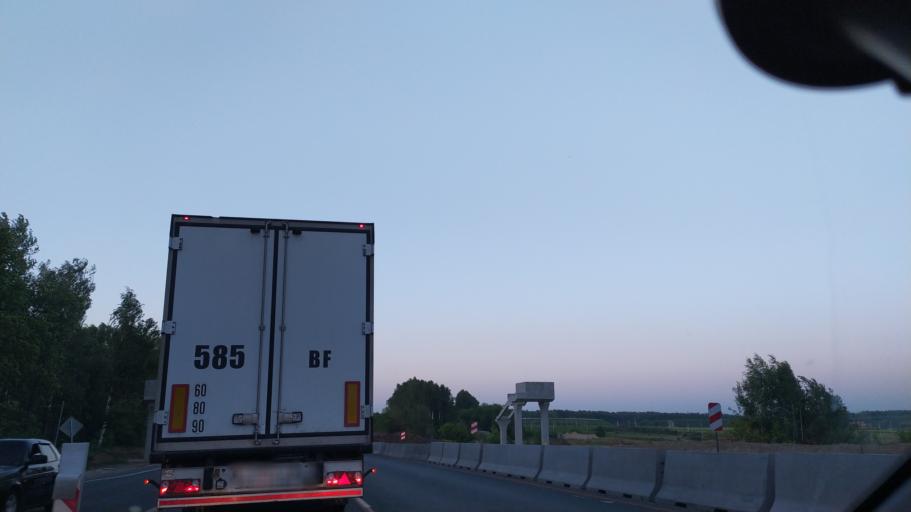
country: RU
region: Chuvashia
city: Ishley
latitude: 56.1043
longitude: 47.0403
